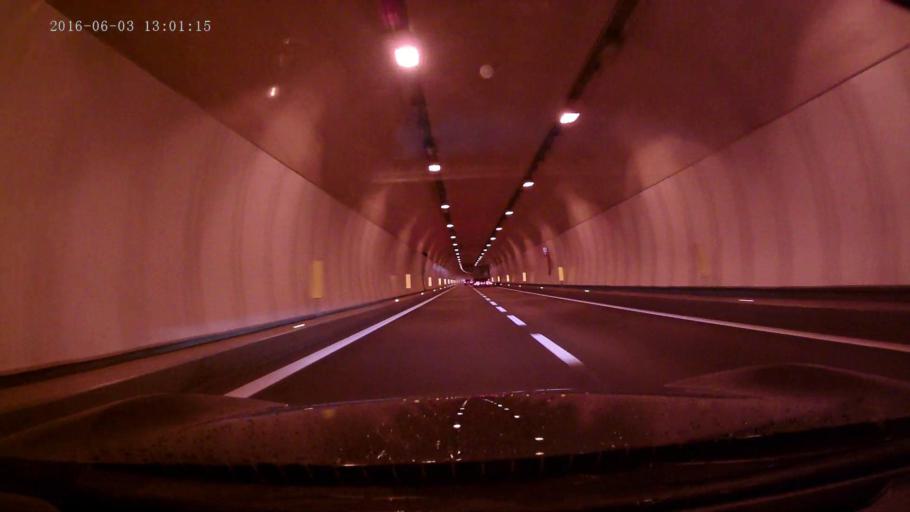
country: IT
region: Trentino-Alto Adige
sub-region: Bolzano
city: Fortezza
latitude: 46.7901
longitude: 11.6127
